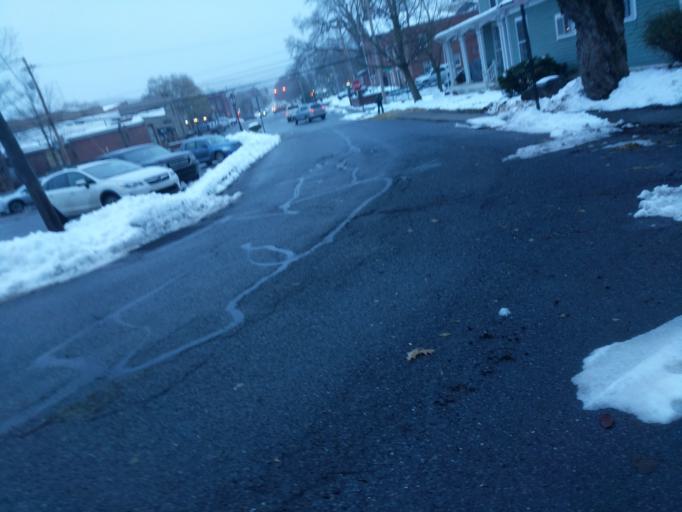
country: US
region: Pennsylvania
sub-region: Tioga County
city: Wellsboro
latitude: 41.7485
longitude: -77.3032
